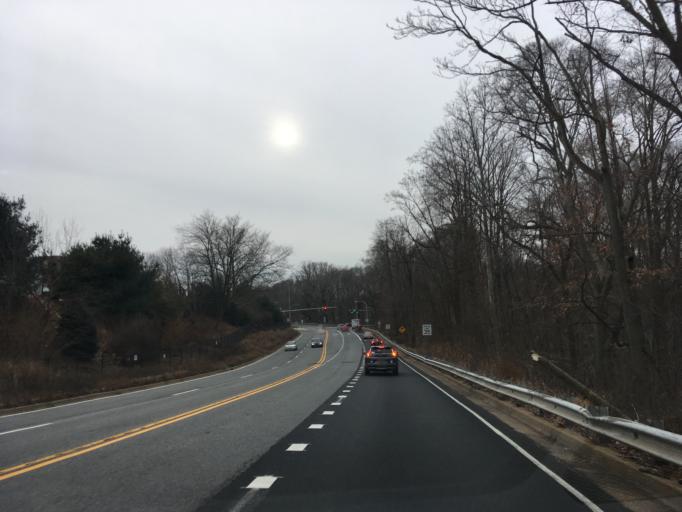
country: US
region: Delaware
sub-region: New Castle County
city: Greenville
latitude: 39.7747
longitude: -75.5749
